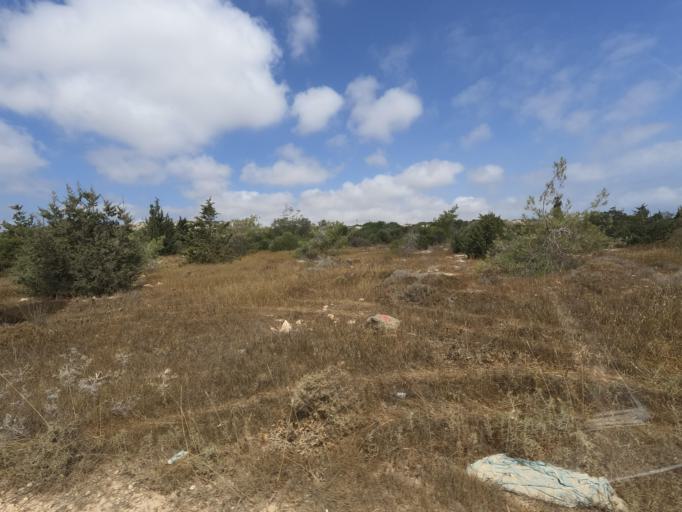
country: CY
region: Ammochostos
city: Protaras
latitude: 35.0044
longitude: 34.0410
